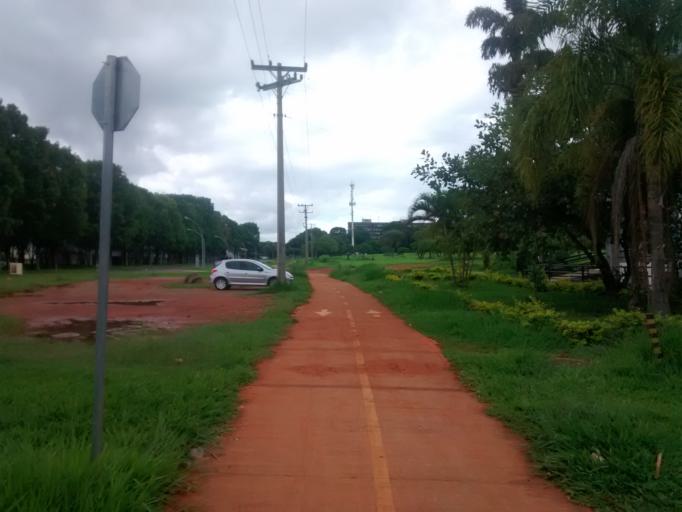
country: BR
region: Federal District
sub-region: Brasilia
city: Brasilia
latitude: -15.7635
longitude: -47.8803
